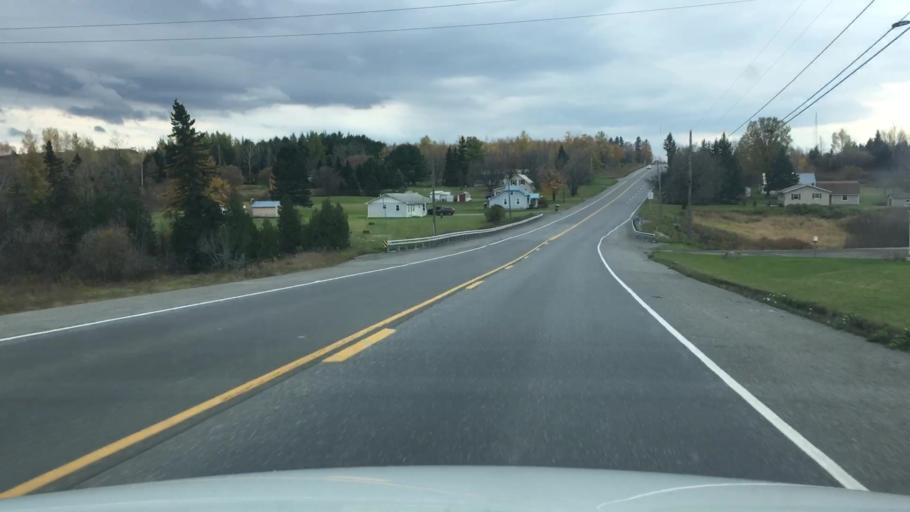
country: US
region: Maine
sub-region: Aroostook County
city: Caribou
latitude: 46.7845
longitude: -67.9891
